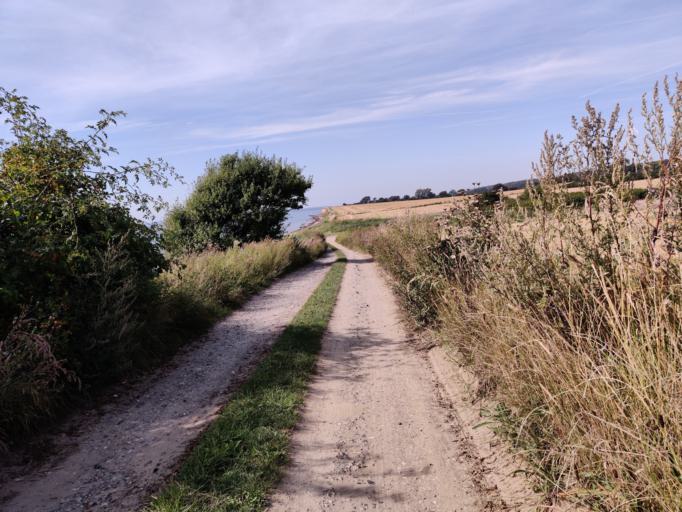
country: DK
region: Zealand
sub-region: Guldborgsund Kommune
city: Nykobing Falster
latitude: 54.6328
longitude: 11.8883
